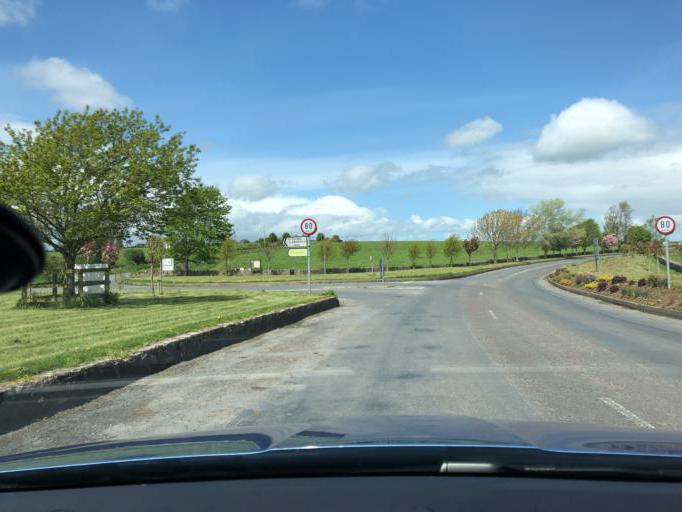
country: IE
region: Munster
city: Cashel
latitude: 52.5217
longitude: -7.8891
